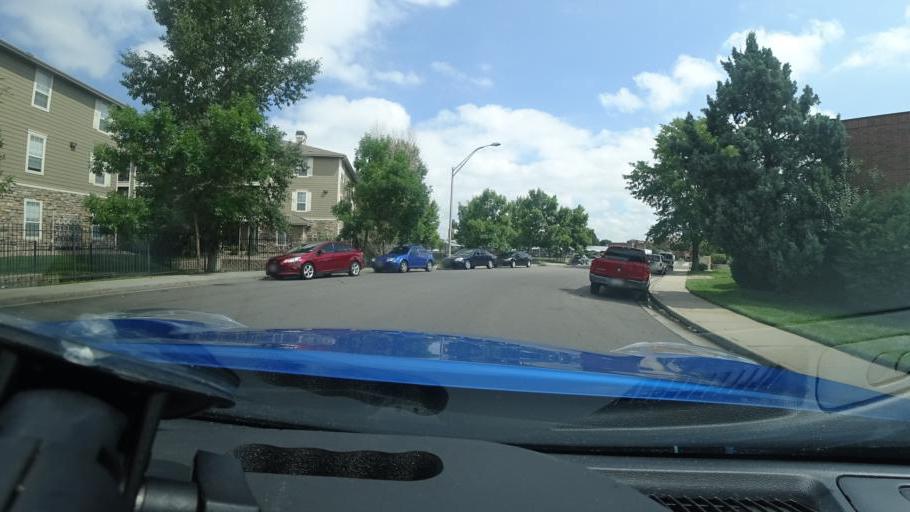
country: US
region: Colorado
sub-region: Adams County
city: Aurora
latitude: 39.7084
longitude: -104.8707
